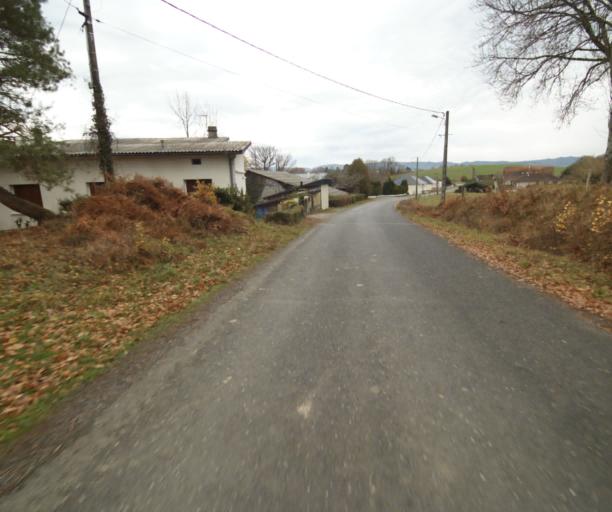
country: FR
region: Limousin
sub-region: Departement de la Correze
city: Tulle
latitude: 45.2549
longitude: 1.7316
